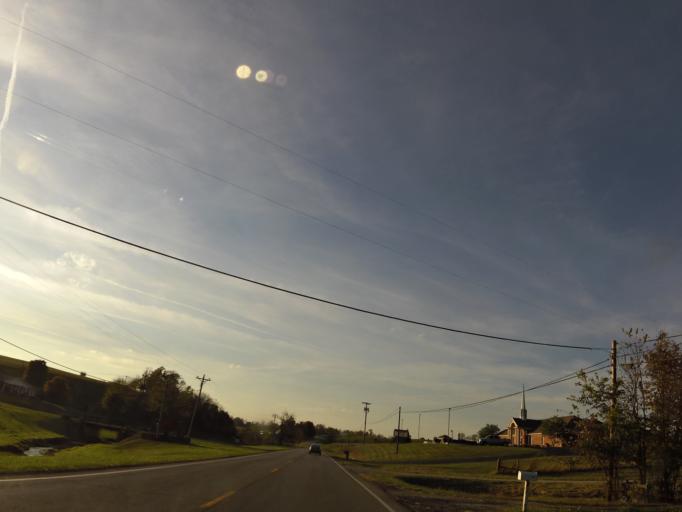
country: US
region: Kentucky
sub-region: Garrard County
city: Lancaster
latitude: 37.6401
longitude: -84.5877
